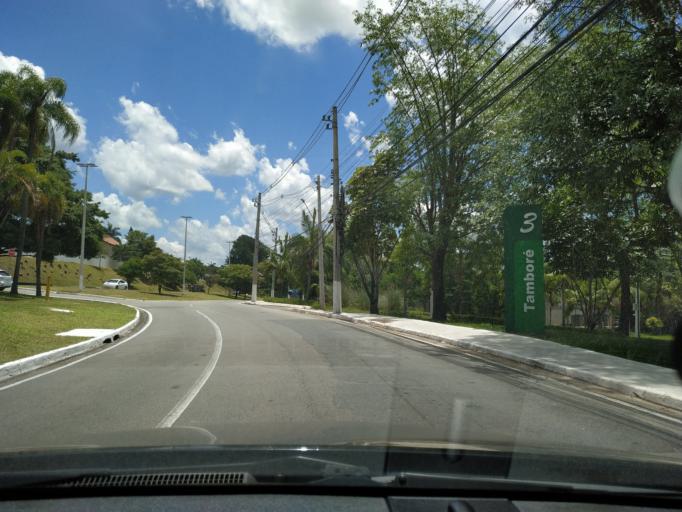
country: BR
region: Sao Paulo
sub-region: Barueri
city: Barueri
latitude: -23.4747
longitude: -46.8619
